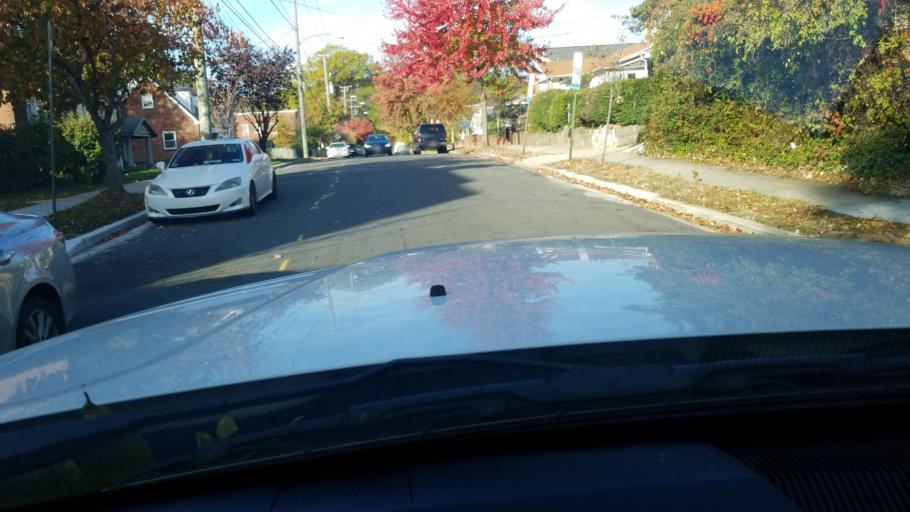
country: US
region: Maryland
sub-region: Prince George's County
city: Fairmount Heights
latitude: 38.8957
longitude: -76.9400
